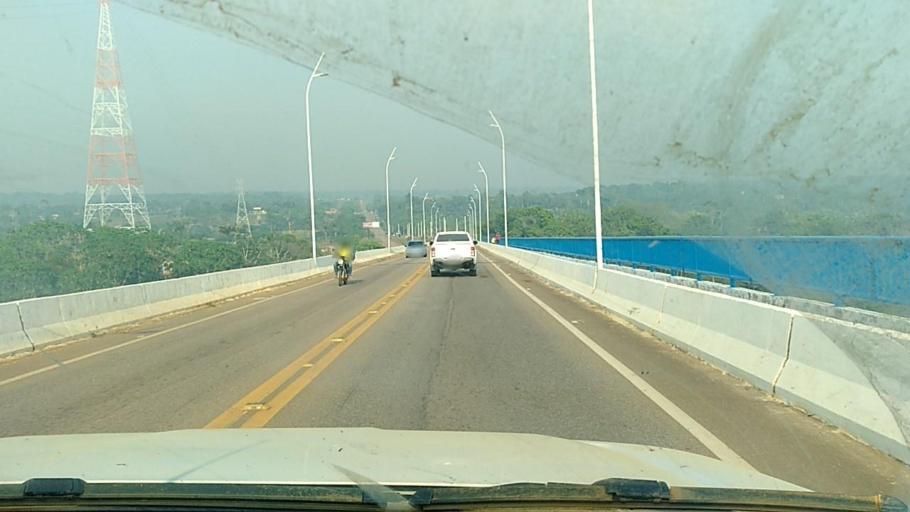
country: BR
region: Rondonia
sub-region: Porto Velho
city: Porto Velho
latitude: -8.7382
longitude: -63.9238
